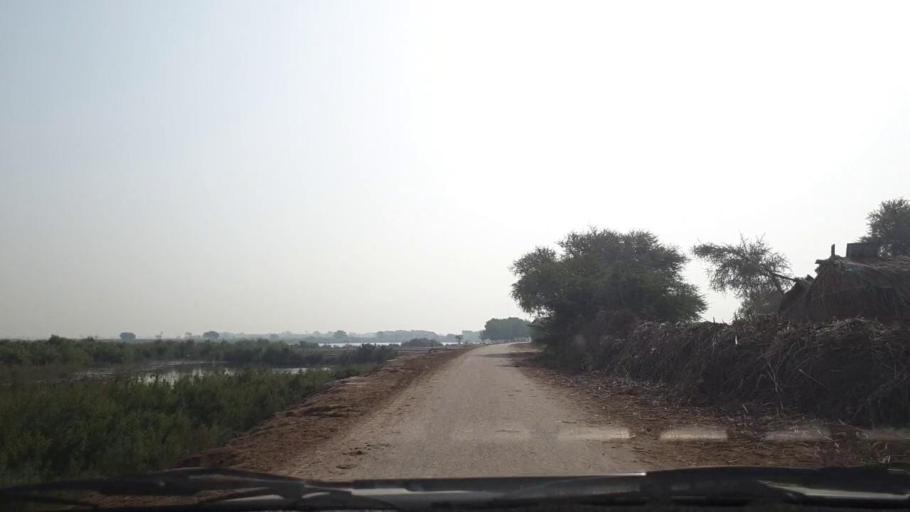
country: PK
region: Sindh
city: Tando Muhammad Khan
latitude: 25.0061
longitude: 68.4507
